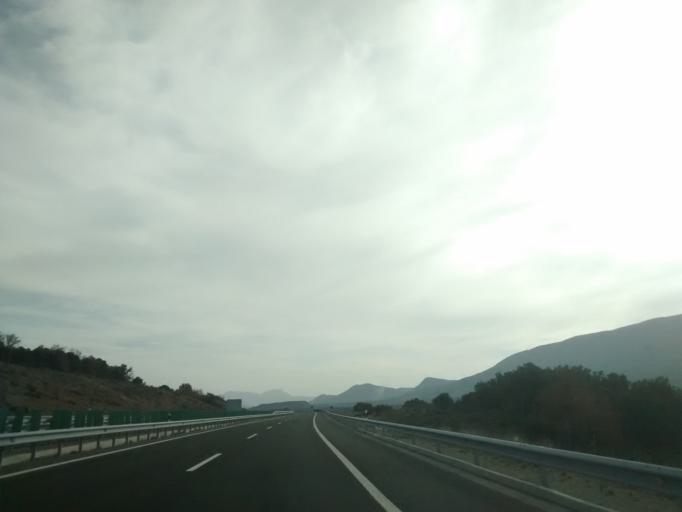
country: ES
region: Aragon
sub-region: Provincia de Zaragoza
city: Artieda
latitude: 42.6113
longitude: -0.9873
